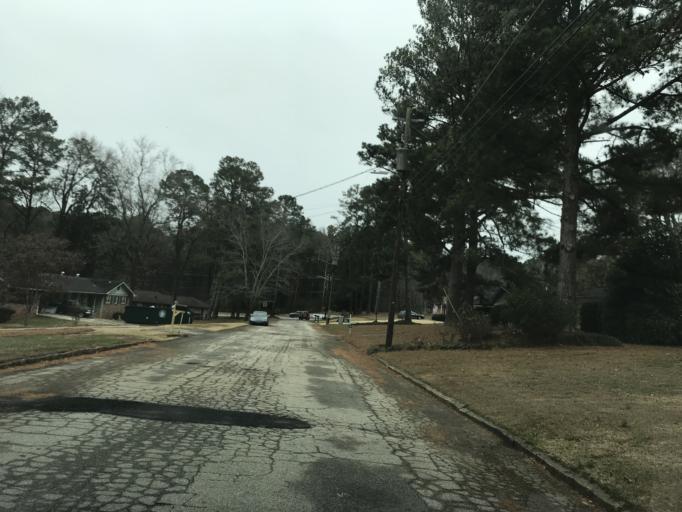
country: US
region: Georgia
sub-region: DeKalb County
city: Clarkston
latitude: 33.8328
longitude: -84.2472
